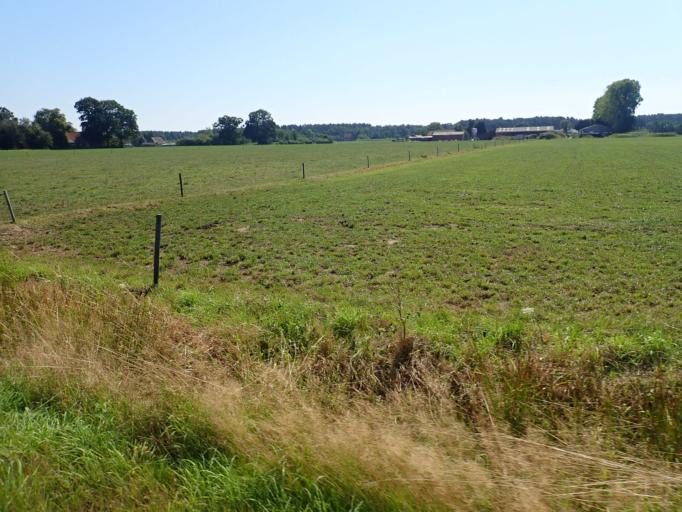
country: BE
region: Flanders
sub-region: Provincie Vlaams-Brabant
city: Scherpenheuvel-Zichem
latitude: 51.0499
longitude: 4.9561
